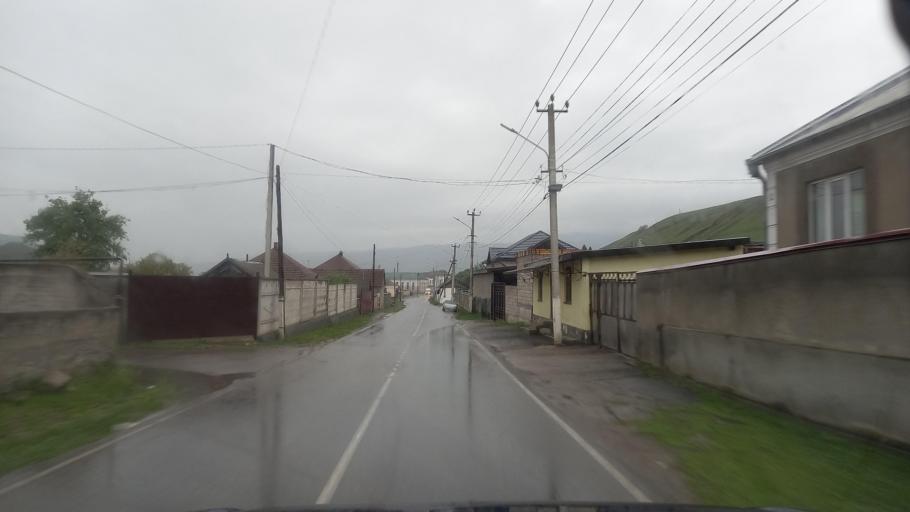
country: RU
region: Kabardino-Balkariya
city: Gundelen
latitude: 43.5944
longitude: 43.1795
